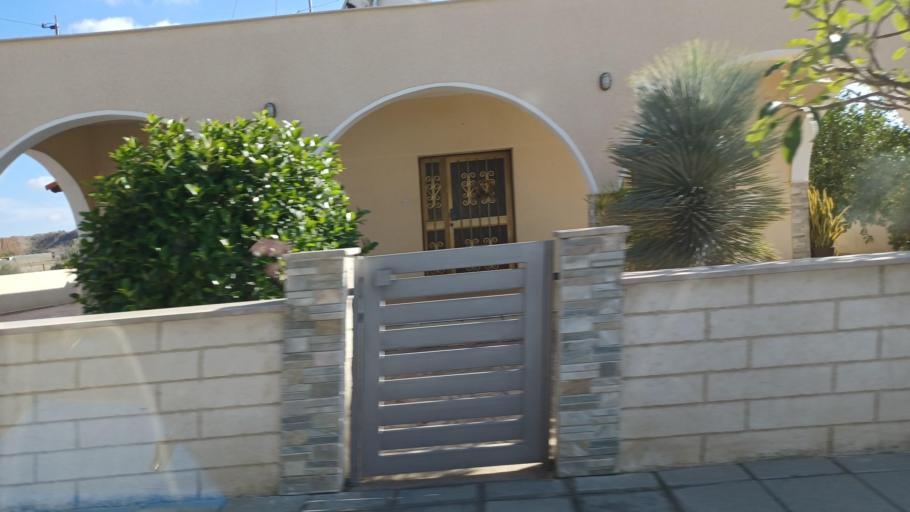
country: CY
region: Larnaka
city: Troulloi
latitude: 35.0289
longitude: 33.6129
